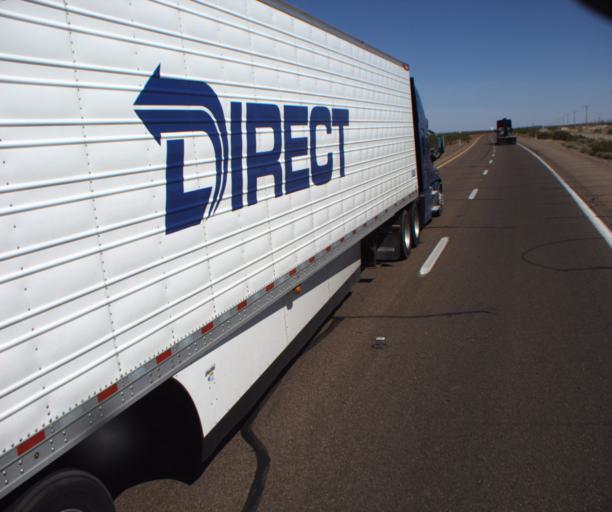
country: US
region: Arizona
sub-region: Yuma County
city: Wellton
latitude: 32.7676
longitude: -113.6164
